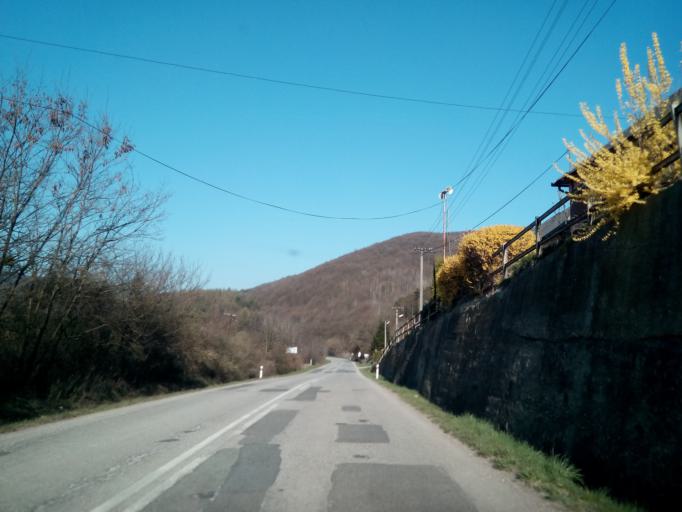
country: SK
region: Kosicky
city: Roznava
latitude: 48.6600
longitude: 20.4830
